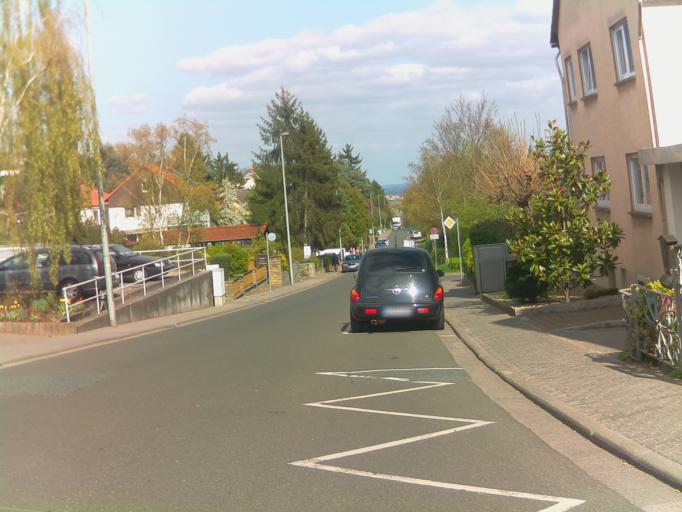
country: DE
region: Rheinland-Pfalz
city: Zornheim
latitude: 49.8903
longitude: 8.2263
